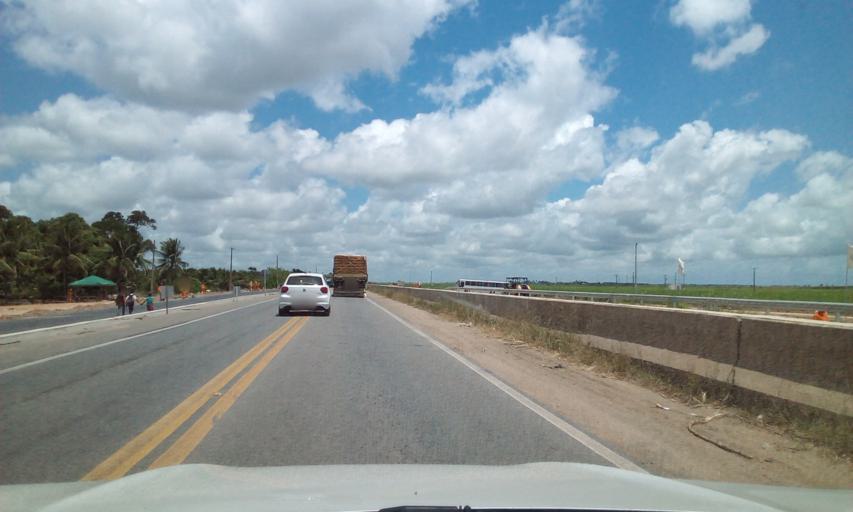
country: BR
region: Alagoas
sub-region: Sao Miguel Dos Campos
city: Sao Miguel dos Campos
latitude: -9.9037
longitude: -36.2171
